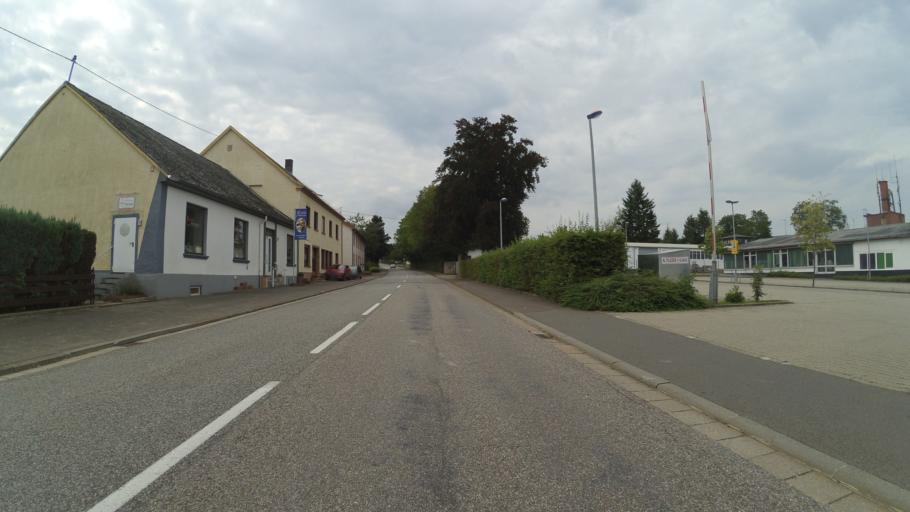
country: DE
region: Saarland
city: Weiskirchen
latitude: 49.5546
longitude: 6.8169
